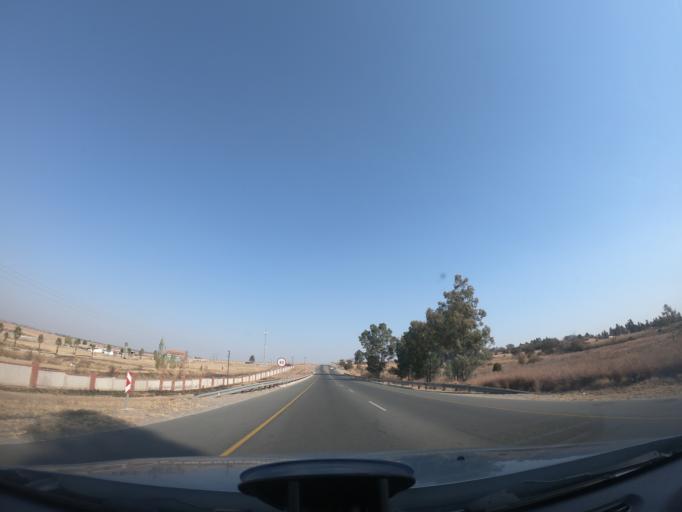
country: ZA
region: Gauteng
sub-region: City of Johannesburg Metropolitan Municipality
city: Diepsloot
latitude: -25.8788
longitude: 28.0276
